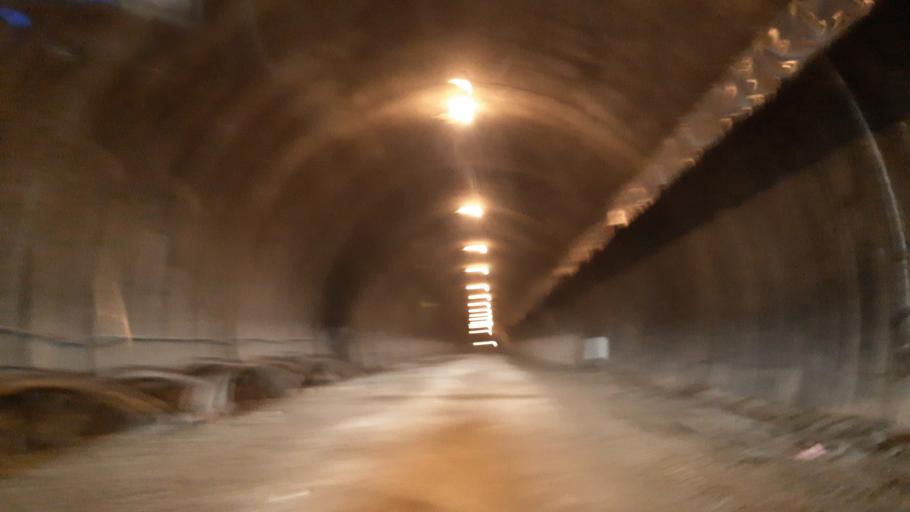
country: KZ
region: Ongtustik Qazaqstan
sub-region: Tulkibas Audany
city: Zhabagly
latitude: 42.5205
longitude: 70.5757
